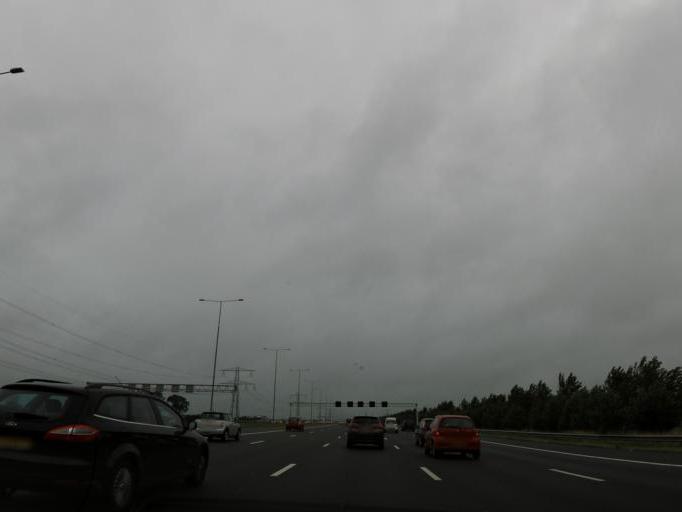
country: NL
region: Utrecht
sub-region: Stichtse Vecht
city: Breukelen
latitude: 52.1949
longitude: 4.9870
